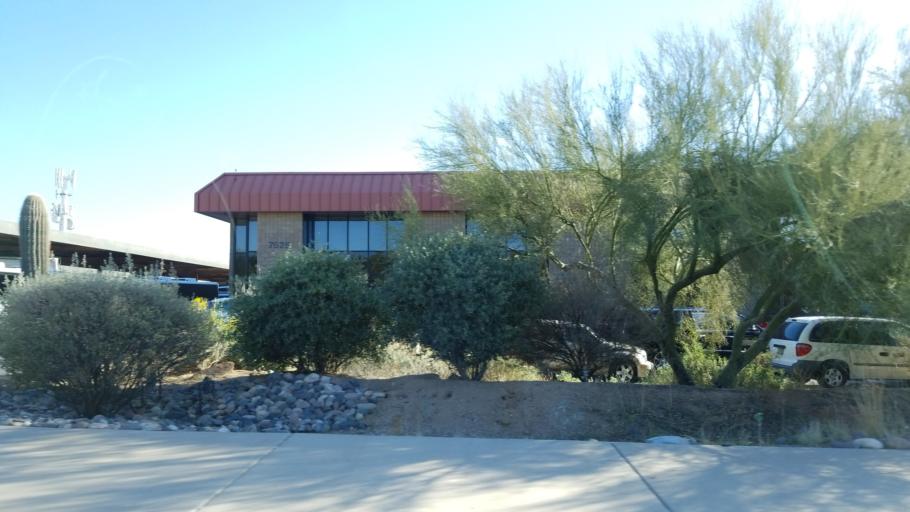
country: US
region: Arizona
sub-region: Maricopa County
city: Carefree
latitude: 33.6914
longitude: -111.9189
